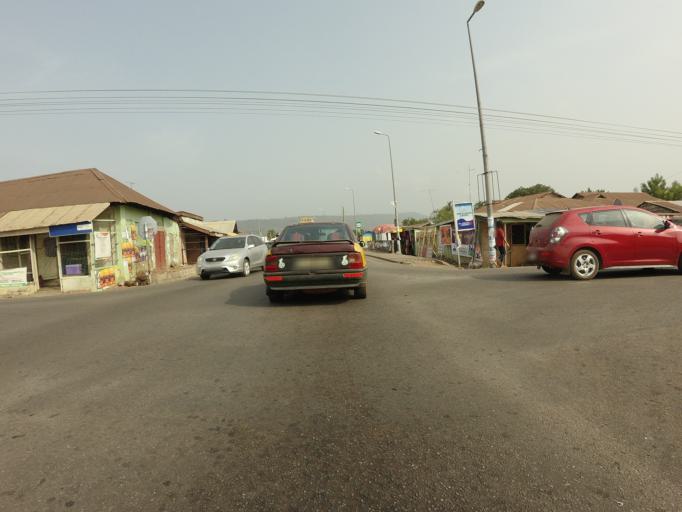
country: GH
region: Volta
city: Ho
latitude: 6.6075
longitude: 0.4750
